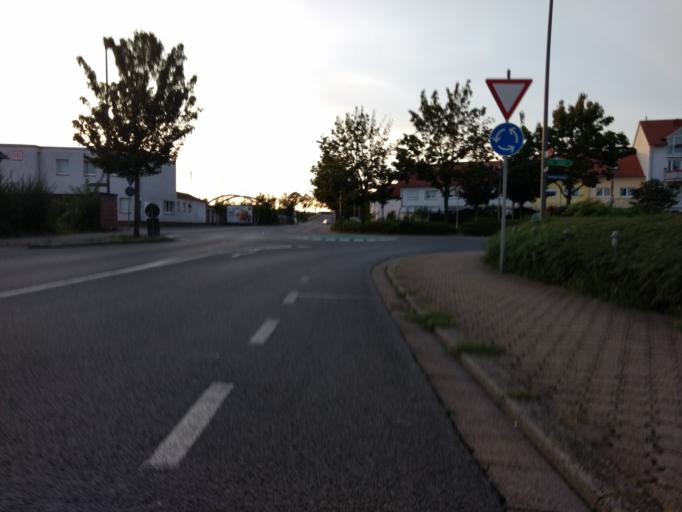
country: DE
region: Saarland
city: Dillingen
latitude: 49.3548
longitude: 6.7205
